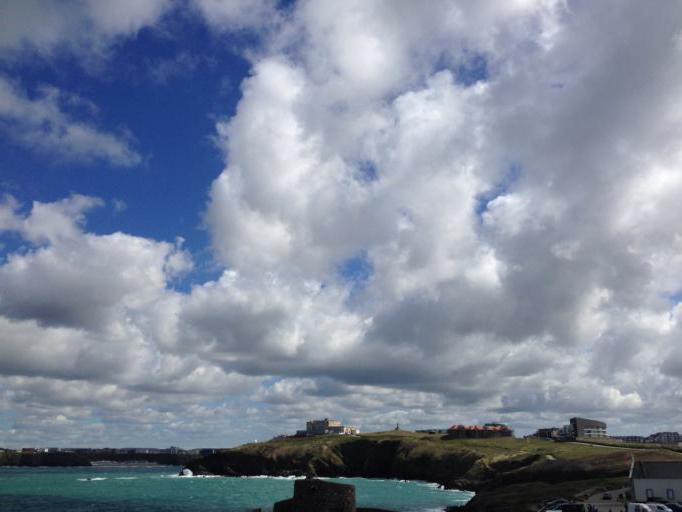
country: GB
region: England
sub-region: Cornwall
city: Newquay
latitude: 50.4243
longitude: -5.0983
